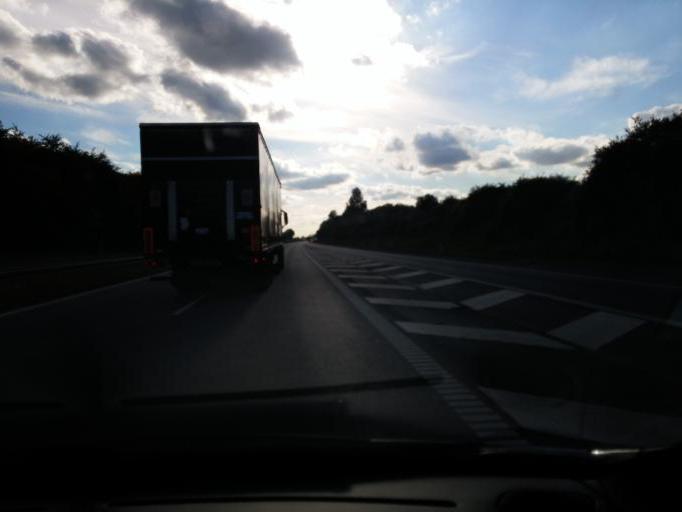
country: DK
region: South Denmark
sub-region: Nyborg Kommune
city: Nyborg
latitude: 55.3322
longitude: 10.7333
